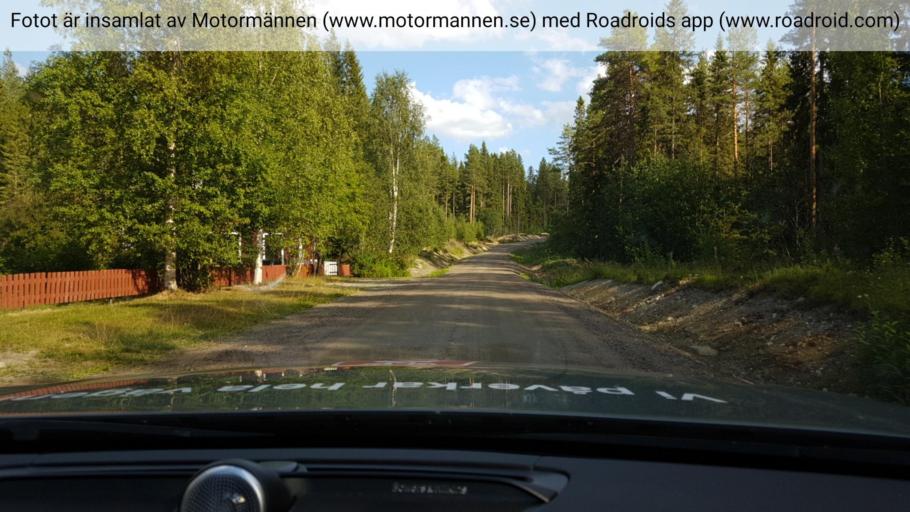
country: SE
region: Vaesterbotten
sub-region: Dorotea Kommun
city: Dorotea
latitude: 63.9418
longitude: 16.0822
